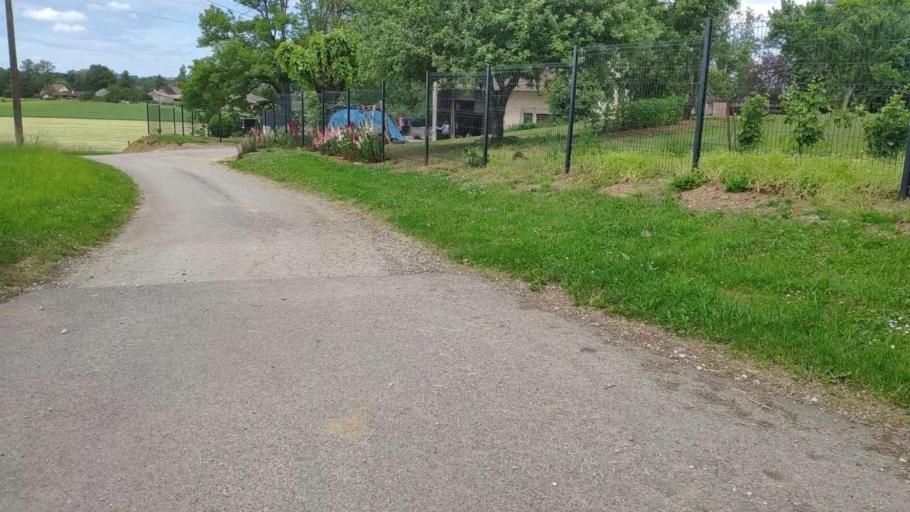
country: FR
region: Franche-Comte
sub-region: Departement du Jura
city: Bletterans
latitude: 46.7324
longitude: 5.4976
